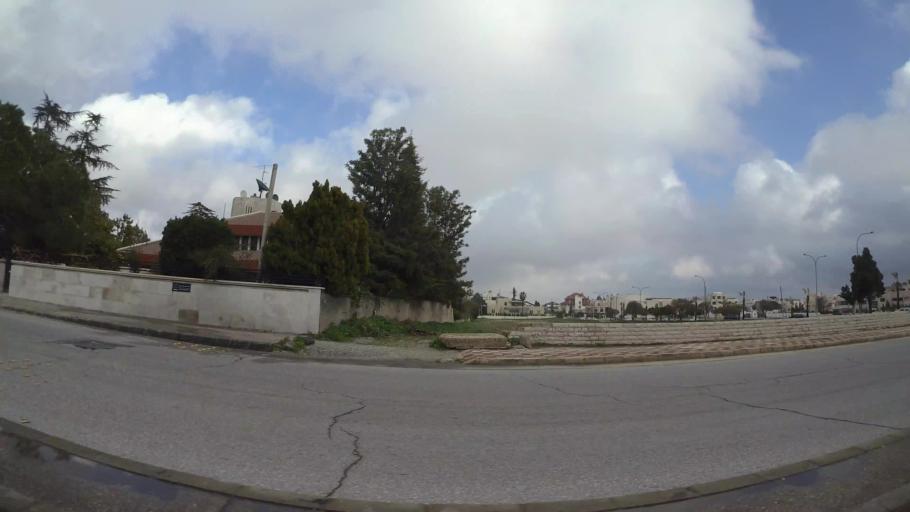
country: JO
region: Amman
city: Wadi as Sir
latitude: 31.9545
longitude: 35.8775
